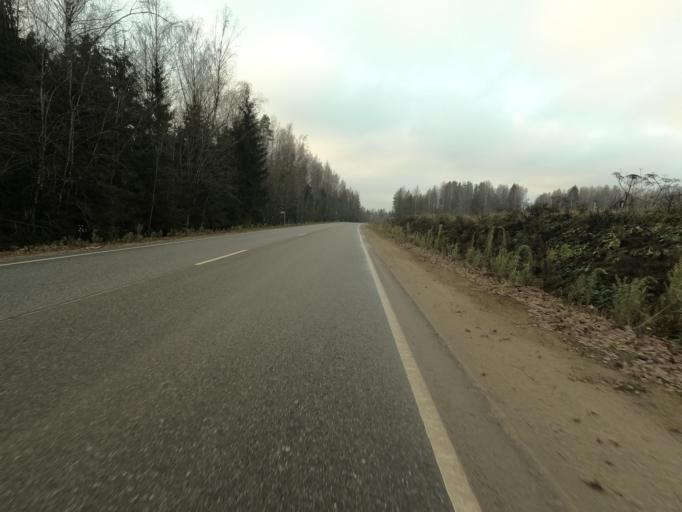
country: RU
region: Leningrad
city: Kirovsk
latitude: 59.8026
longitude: 30.9786
